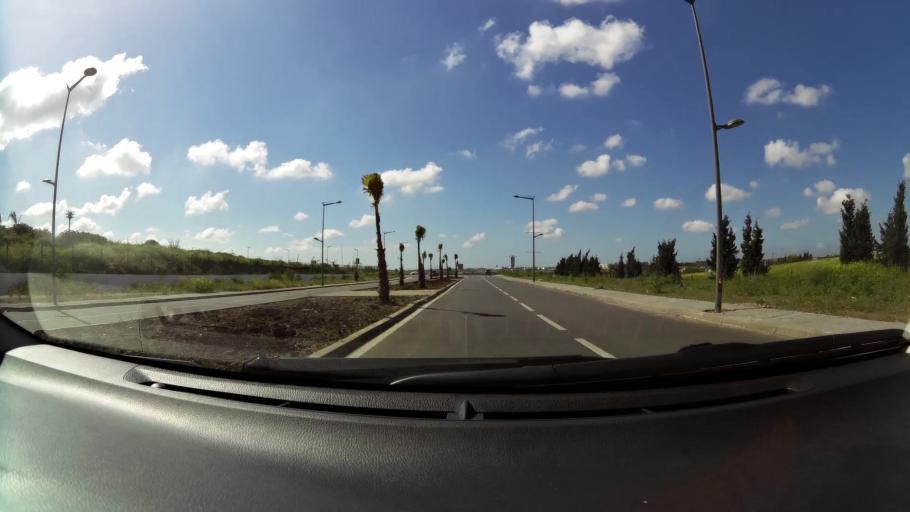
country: MA
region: Grand Casablanca
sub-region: Nouaceur
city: Bouskoura
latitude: 33.4764
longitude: -7.6034
